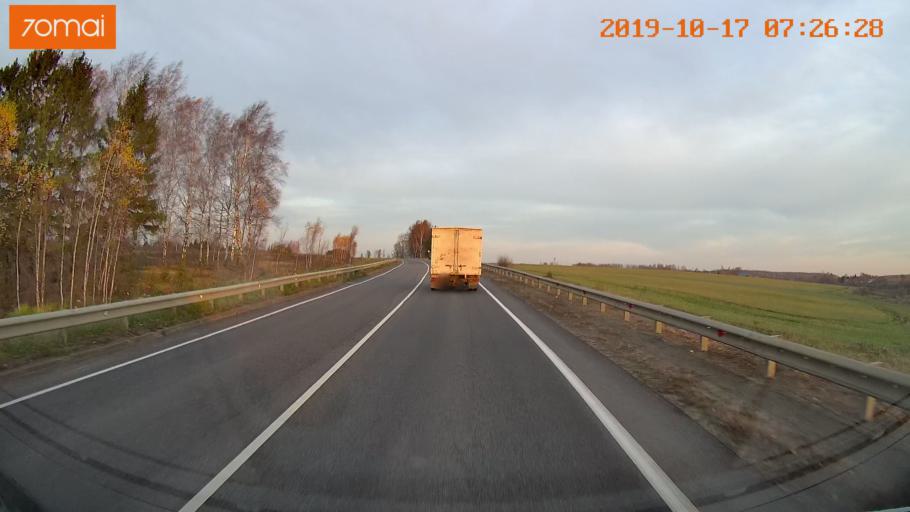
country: RU
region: Ivanovo
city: Gavrilov Posad
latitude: 56.3575
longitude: 40.0921
